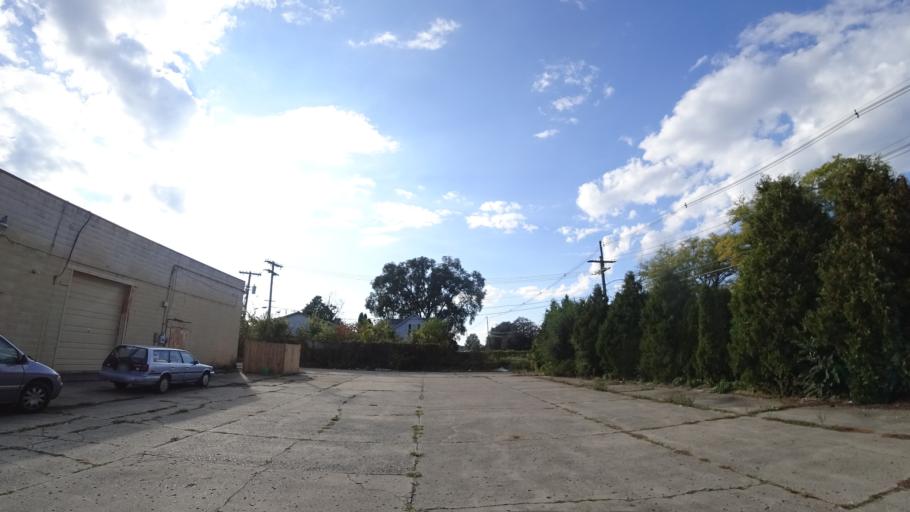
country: US
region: Michigan
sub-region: Saint Joseph County
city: Sturgis
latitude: 41.7990
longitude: -85.4297
